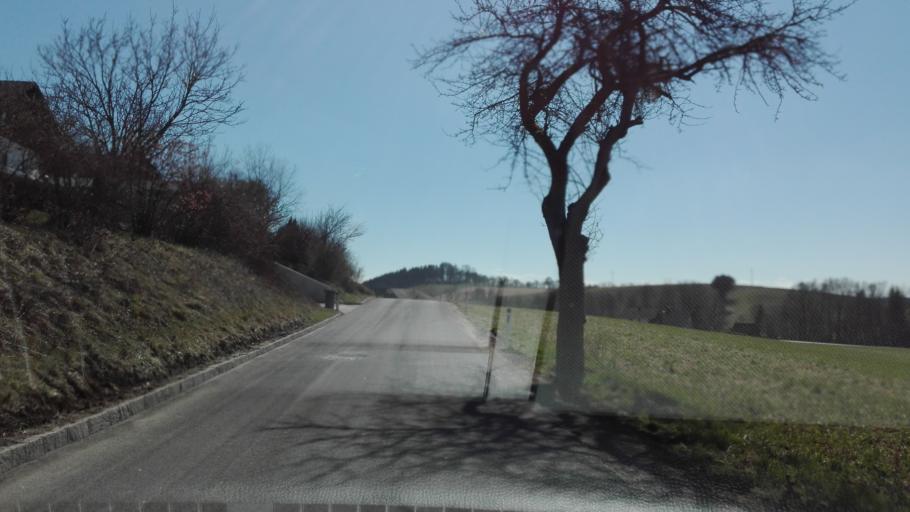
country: AT
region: Upper Austria
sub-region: Wels-Land
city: Buchkirchen
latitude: 48.2294
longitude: 13.9741
